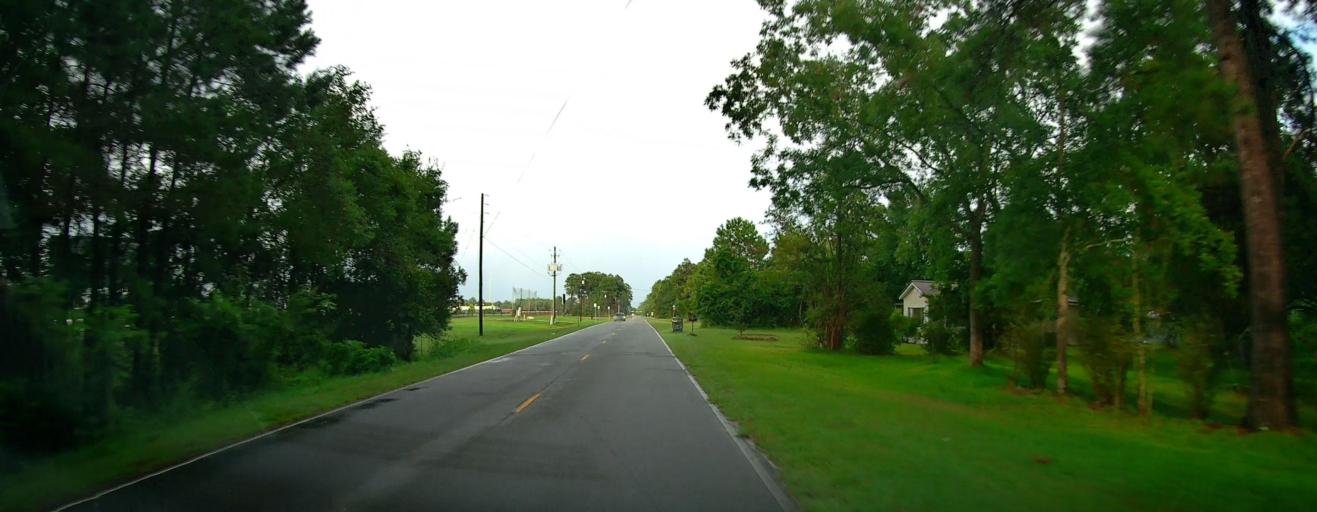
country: US
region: Georgia
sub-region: Ware County
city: Deenwood
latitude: 31.1950
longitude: -82.3948
